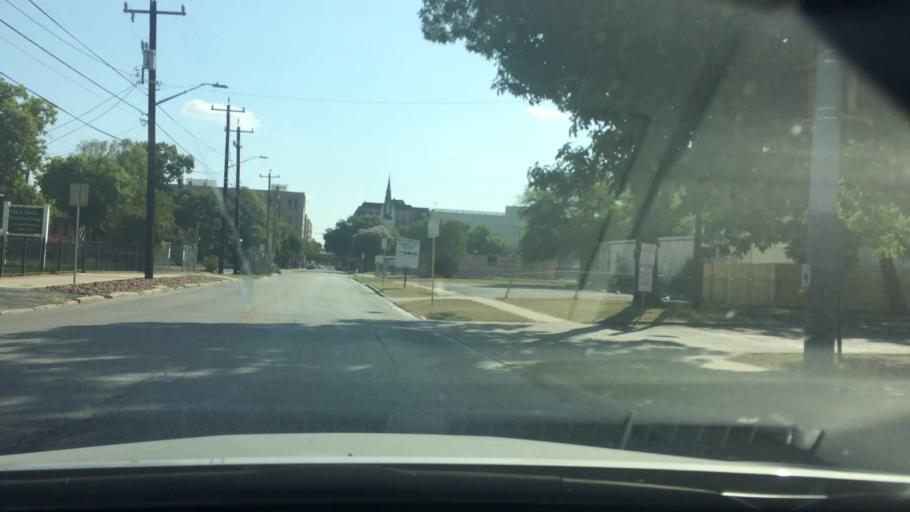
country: US
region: Texas
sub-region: Bexar County
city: San Antonio
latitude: 29.4362
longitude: -98.4894
